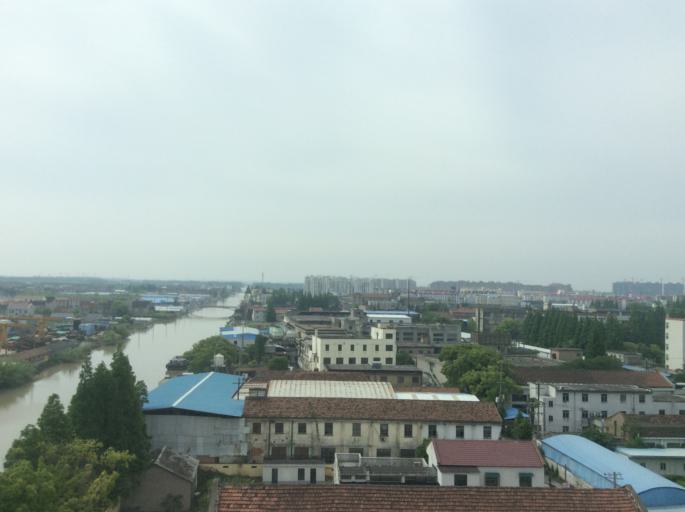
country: CN
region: Shanghai Shi
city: Kangqiao
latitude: 31.2029
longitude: 121.7031
